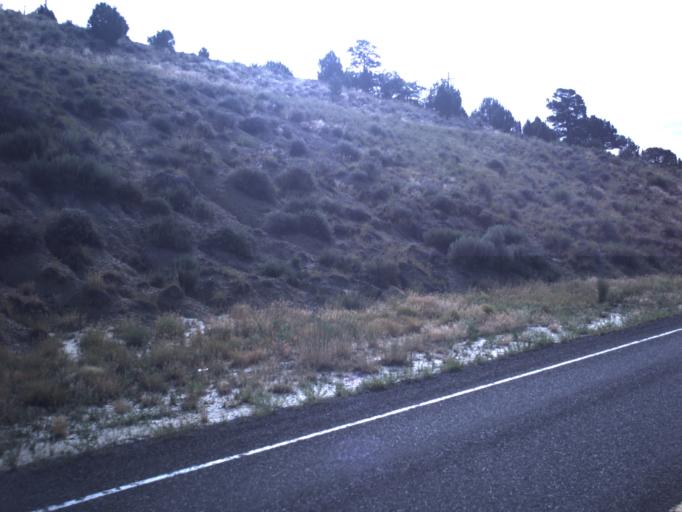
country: US
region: Utah
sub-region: Washington County
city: Hildale
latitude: 37.2612
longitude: -112.7701
